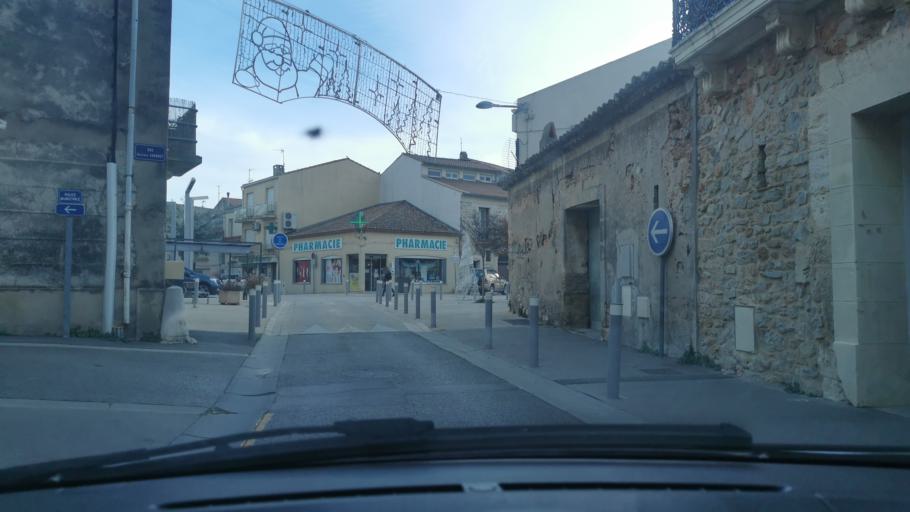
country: FR
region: Languedoc-Roussillon
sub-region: Departement de l'Herault
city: Mireval
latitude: 43.5082
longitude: 3.8012
